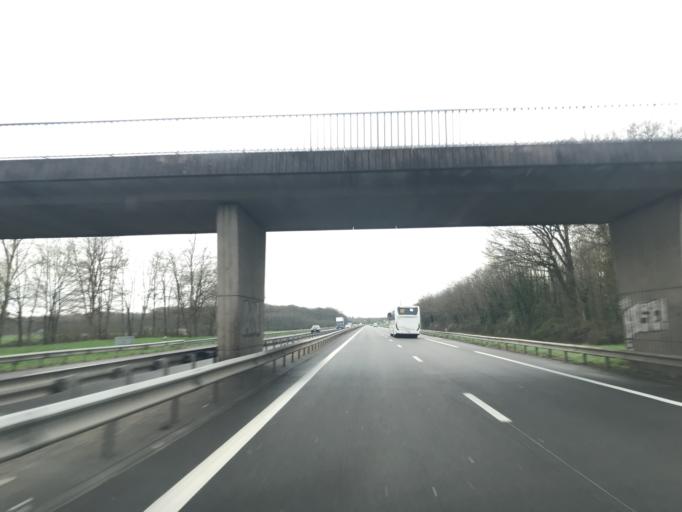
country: FR
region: Centre
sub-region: Departement du Loiret
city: Mardie
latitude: 47.9072
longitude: 2.0530
